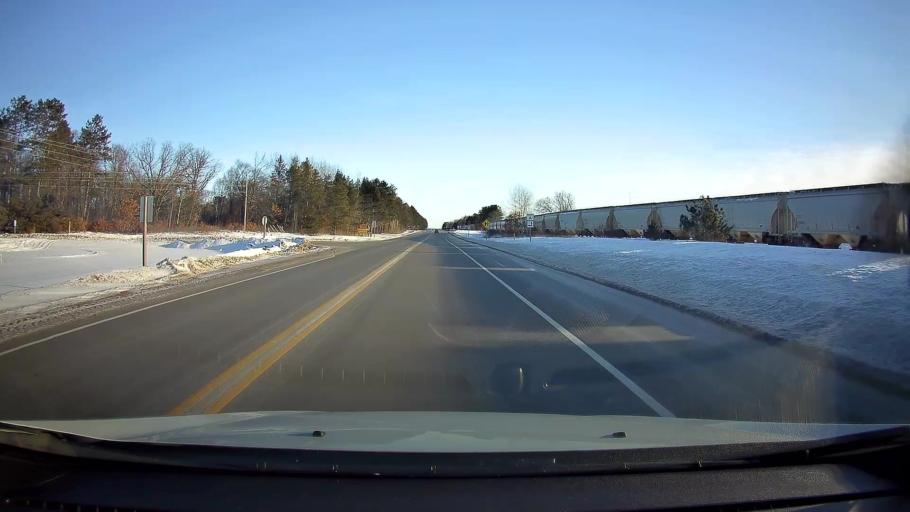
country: US
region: Wisconsin
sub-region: Washburn County
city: Spooner
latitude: 45.8427
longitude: -91.8757
